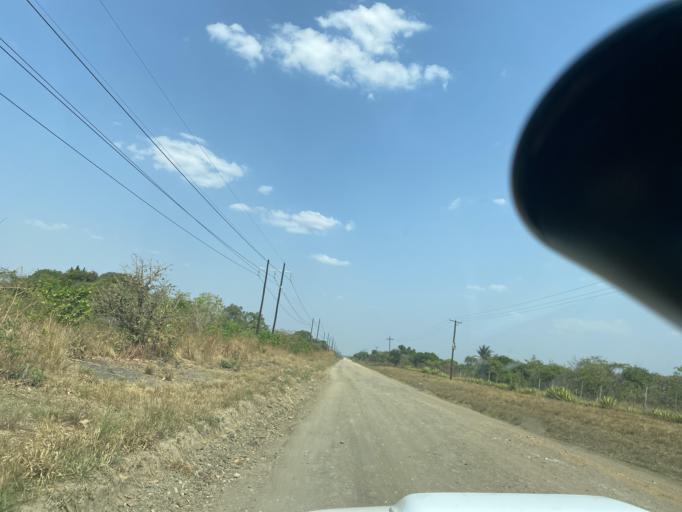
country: ZM
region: Lusaka
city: Lusaka
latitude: -15.3052
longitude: 28.0376
